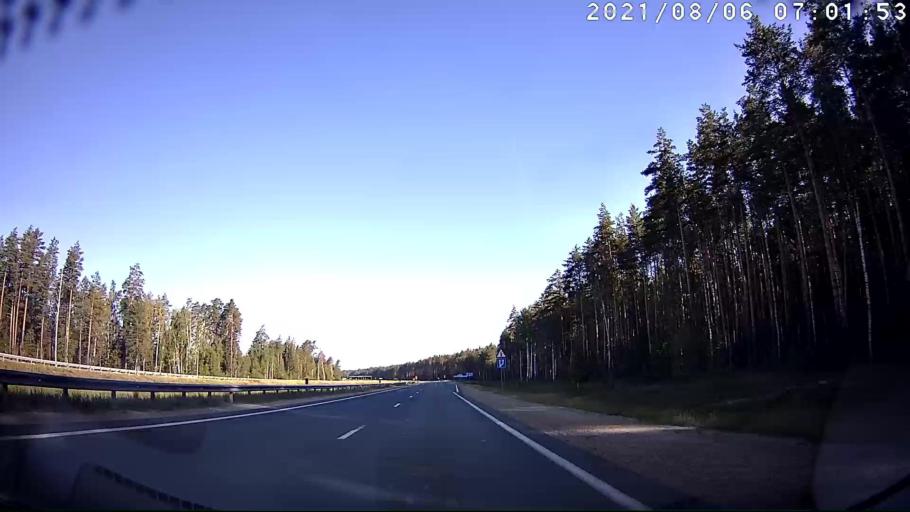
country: RU
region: Mariy-El
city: Surok
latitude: 56.5283
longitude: 48.0046
